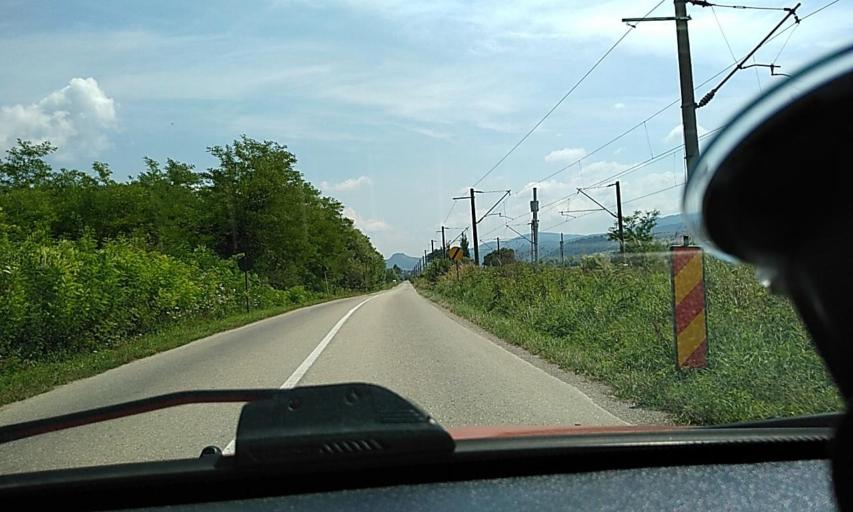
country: RO
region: Brasov
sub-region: Comuna Hoghiz
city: Hoghiz
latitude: 46.0291
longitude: 25.3674
